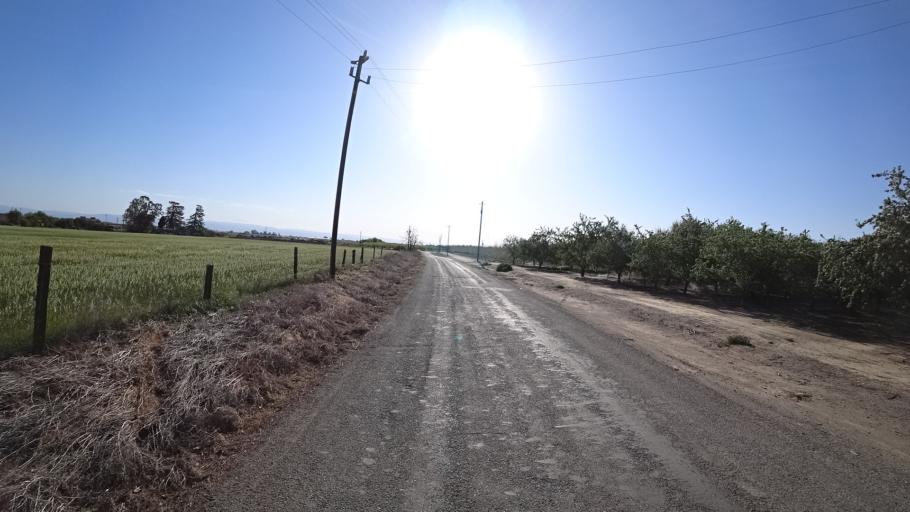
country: US
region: California
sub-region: Glenn County
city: Orland
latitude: 39.7146
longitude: -122.1628
